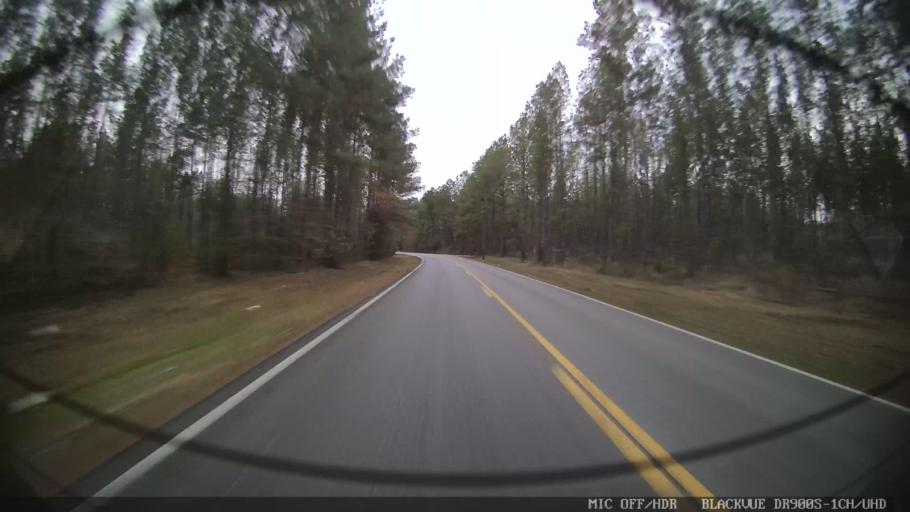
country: US
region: Mississippi
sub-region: Clarke County
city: Quitman
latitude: 32.0293
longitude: -88.8305
